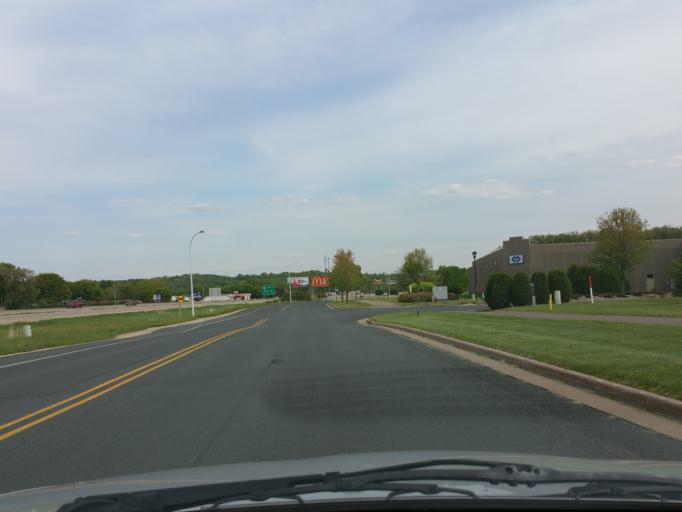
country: US
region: Wisconsin
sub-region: Pierce County
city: River Falls
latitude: 44.8883
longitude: -92.6314
